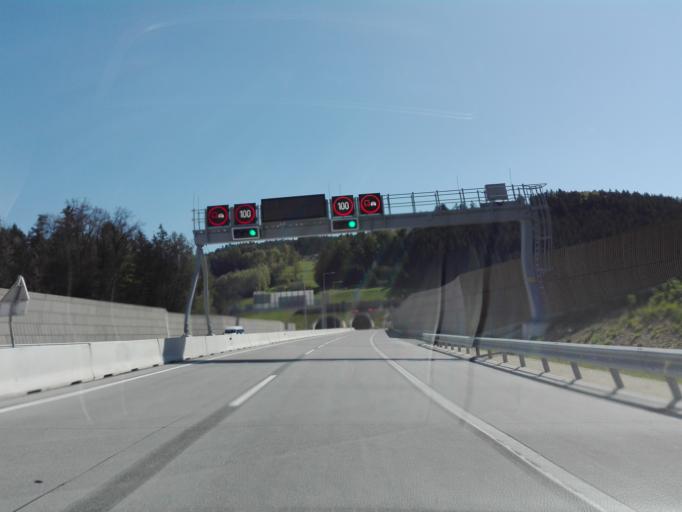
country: AT
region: Upper Austria
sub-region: Politischer Bezirk Urfahr-Umgebung
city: Alberndorf in der Riedmark
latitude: 48.4120
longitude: 14.4844
